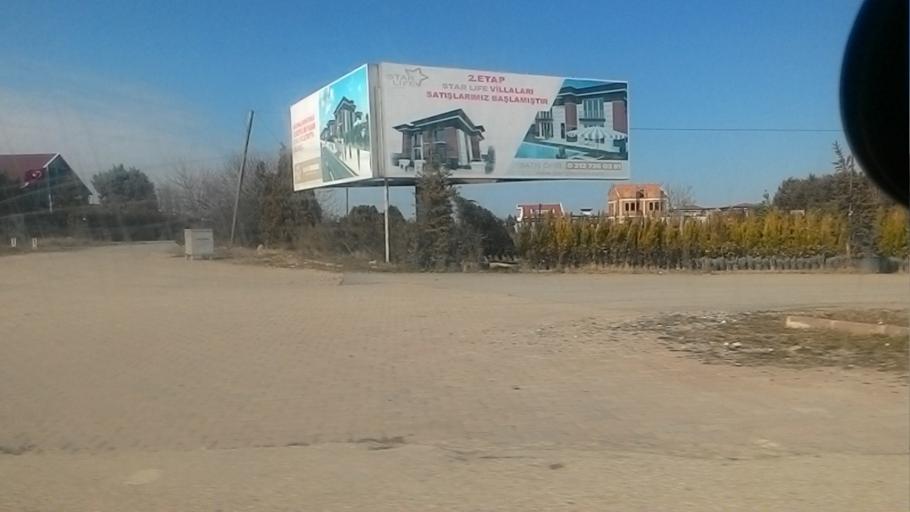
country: TR
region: Istanbul
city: Silivri
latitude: 41.0797
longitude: 28.1974
